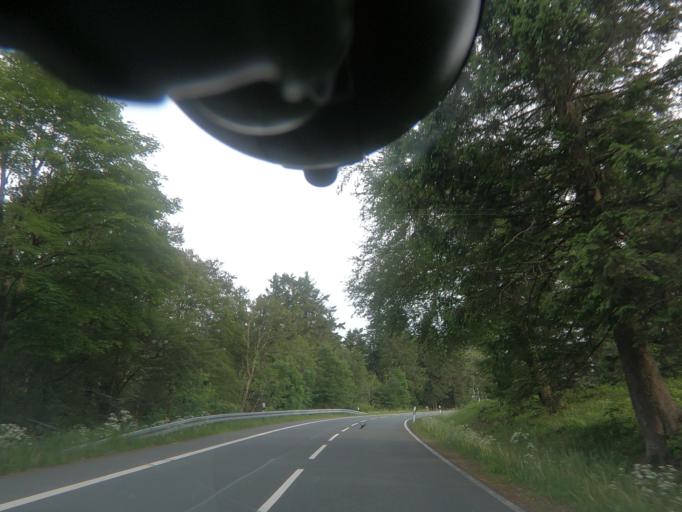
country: DE
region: North Rhine-Westphalia
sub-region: Regierungsbezirk Arnsberg
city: Winterberg
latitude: 51.1810
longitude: 8.4914
